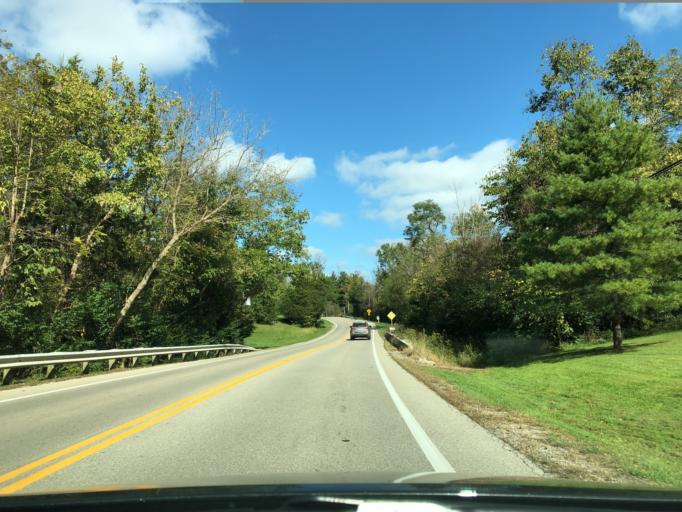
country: US
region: Ohio
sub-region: Hamilton County
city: Loveland
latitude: 39.2776
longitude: -84.2443
